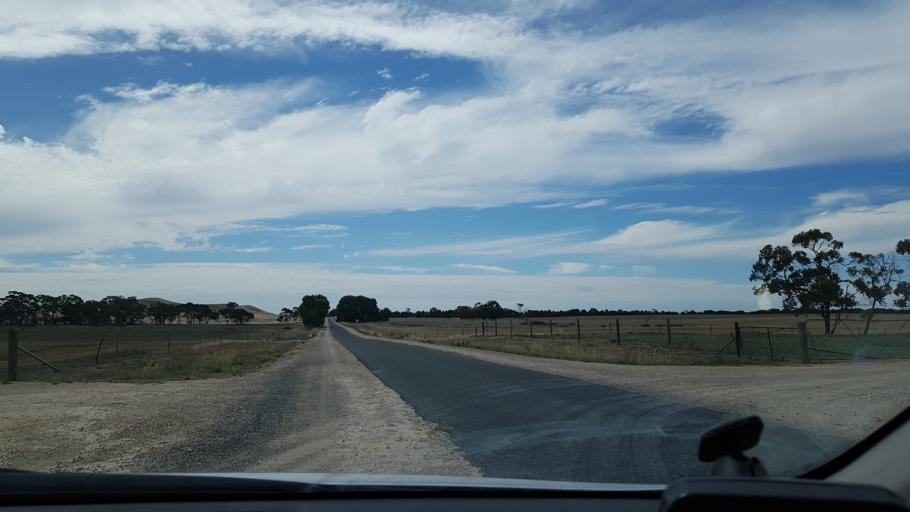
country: AU
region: Victoria
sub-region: Horsham
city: Horsham
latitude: -36.7192
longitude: 141.7783
